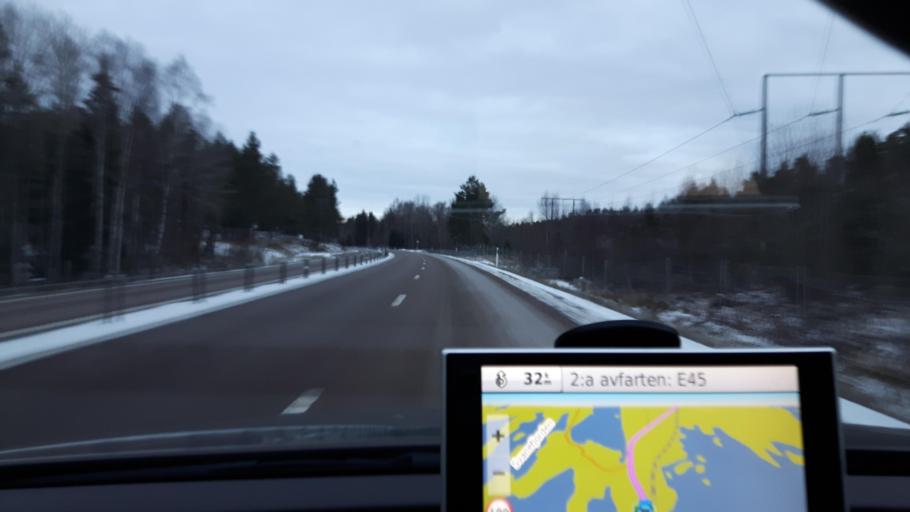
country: SE
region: Vaestra Goetaland
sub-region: Melleruds Kommun
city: Mellerud
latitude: 58.8042
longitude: 12.5270
